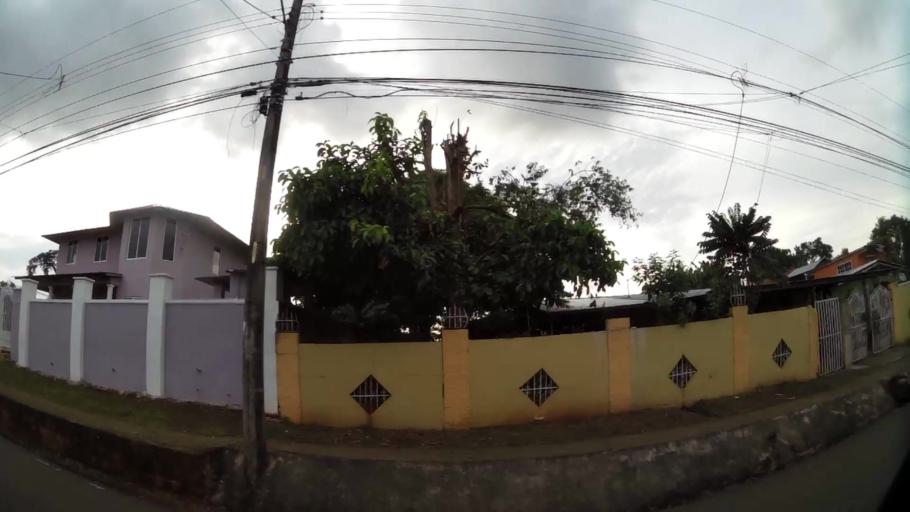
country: PA
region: Panama
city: Tocumen
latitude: 9.0982
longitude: -79.3776
